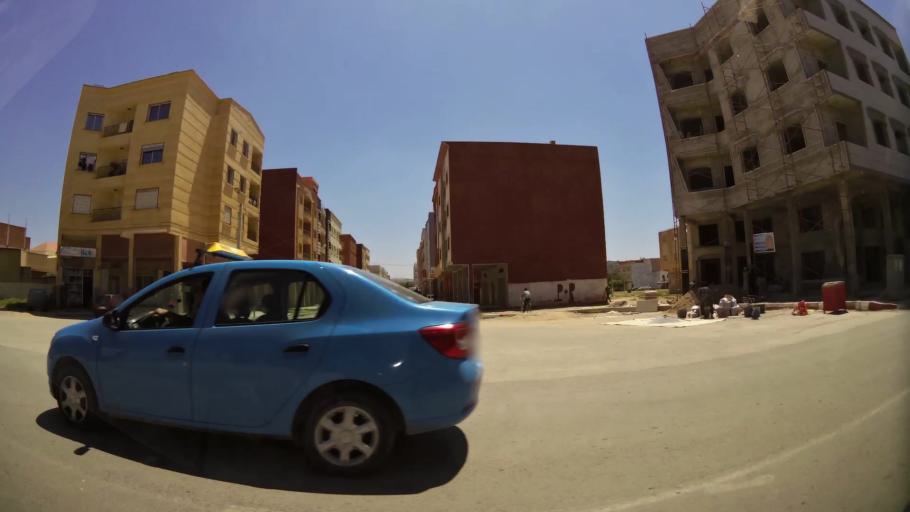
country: MA
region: Oriental
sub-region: Berkane-Taourirt
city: Madagh
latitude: 35.0779
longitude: -2.2236
